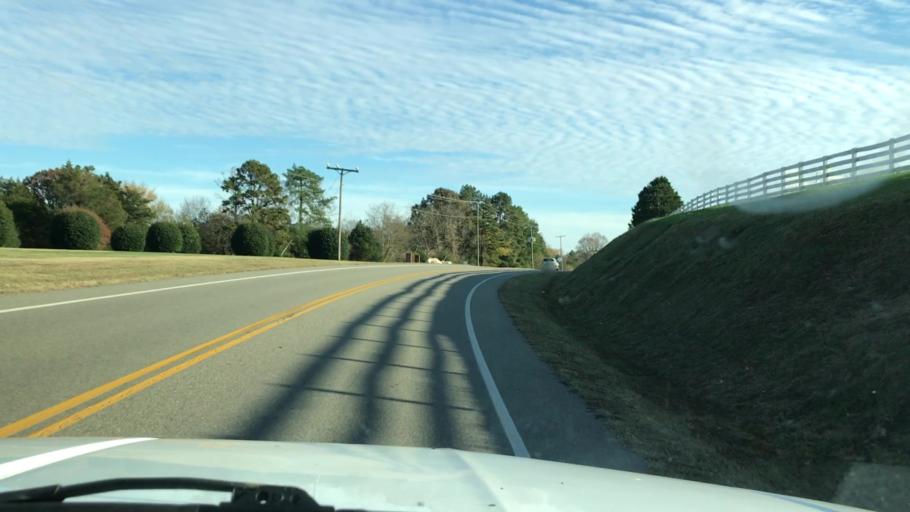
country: US
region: Virginia
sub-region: Goochland County
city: Goochland
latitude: 37.6454
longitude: -77.8184
